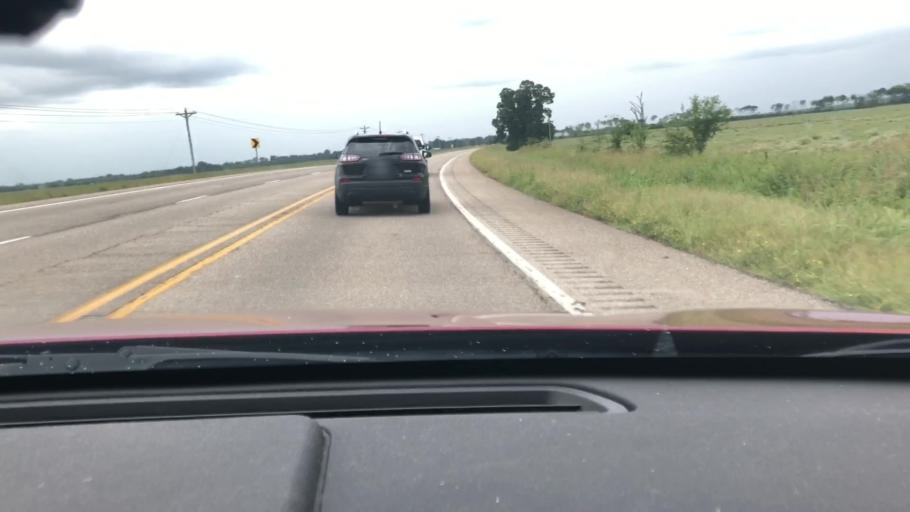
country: US
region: Arkansas
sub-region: Lafayette County
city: Lewisville
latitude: 33.3896
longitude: -93.7364
